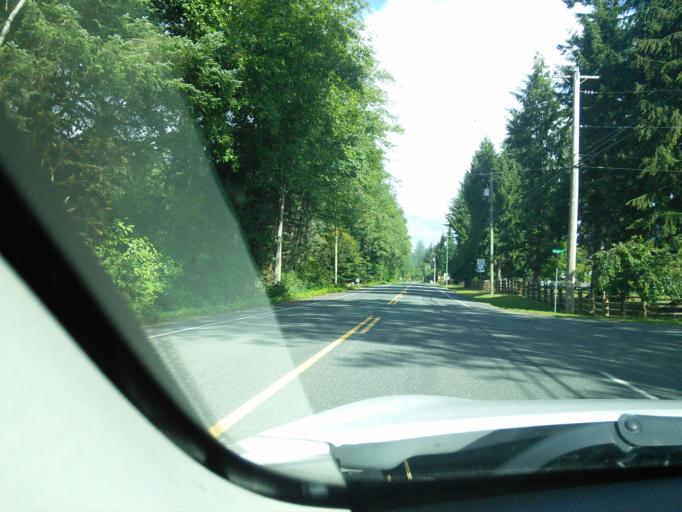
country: CA
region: British Columbia
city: Campbell River
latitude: 50.3139
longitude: -125.9200
